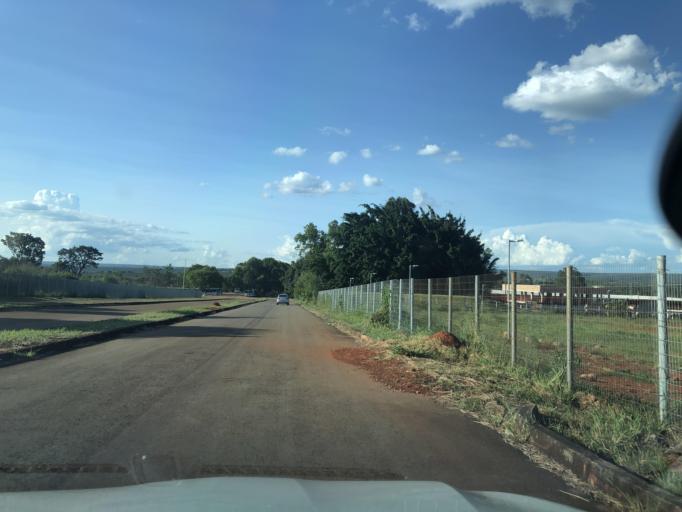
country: BR
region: Federal District
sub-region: Brasilia
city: Brasilia
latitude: -15.7384
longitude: -47.9053
